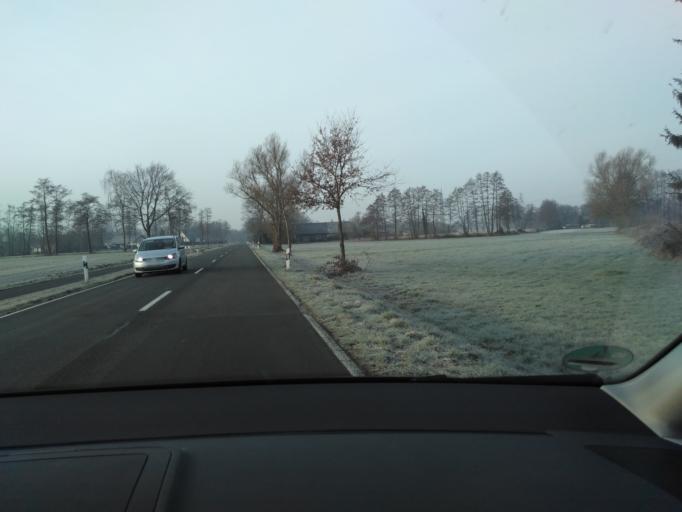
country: DE
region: North Rhine-Westphalia
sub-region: Regierungsbezirk Detmold
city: Verl
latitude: 51.8570
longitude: 8.4883
